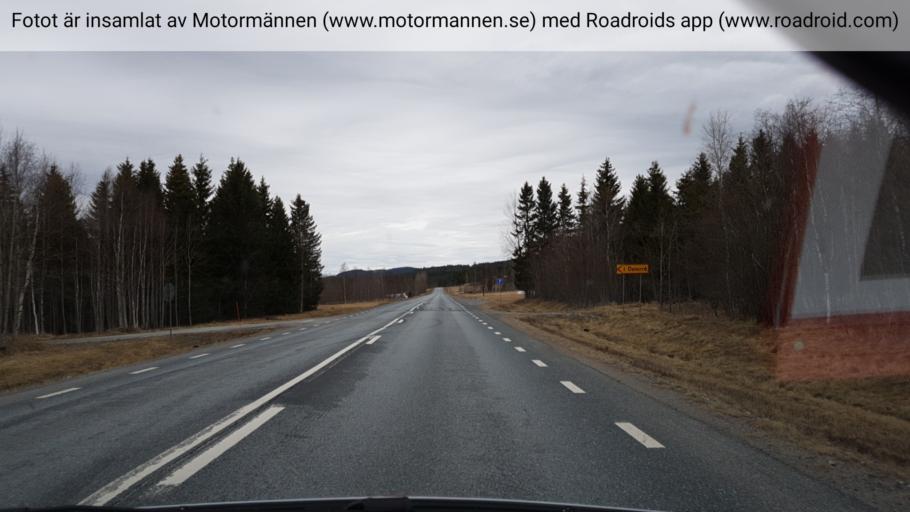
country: SE
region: Vaesternorrland
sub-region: Solleftea Kommun
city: Solleftea
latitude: 63.3248
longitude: 17.1618
